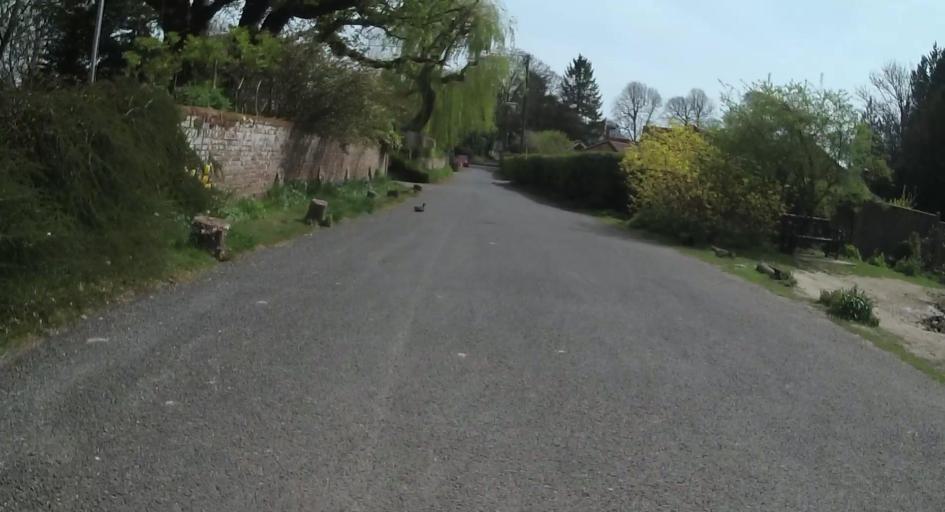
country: GB
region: England
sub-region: Hampshire
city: Alton
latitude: 51.1655
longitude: -0.9531
